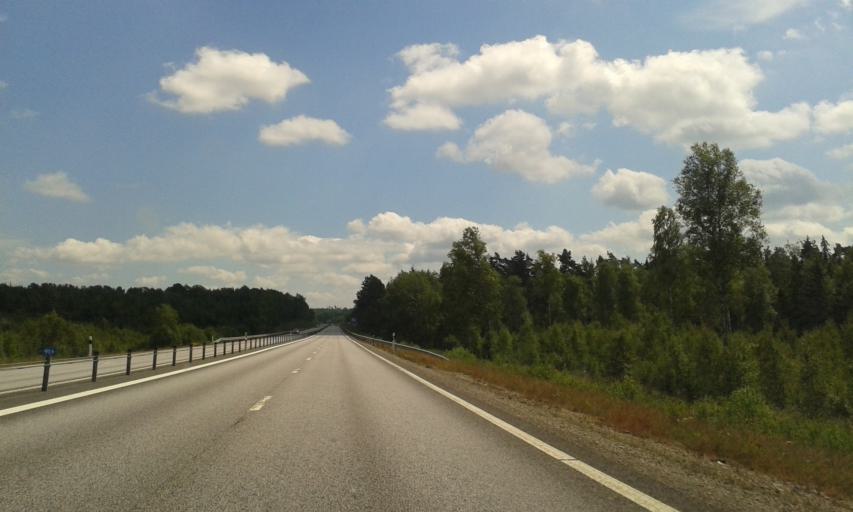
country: SE
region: Kronoberg
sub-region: Vaxjo Kommun
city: Gemla
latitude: 56.9037
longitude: 14.6645
